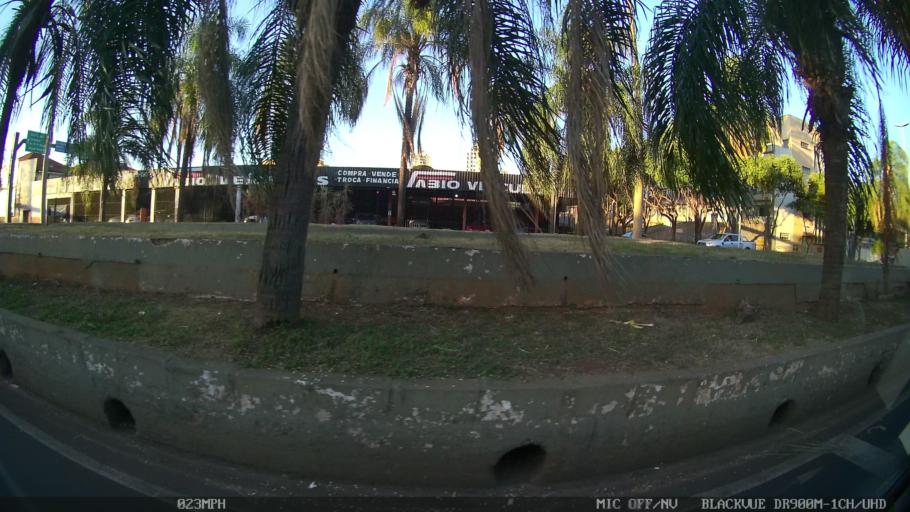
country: BR
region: Sao Paulo
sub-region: Sao Jose Do Rio Preto
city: Sao Jose do Rio Preto
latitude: -20.8082
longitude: -49.3757
